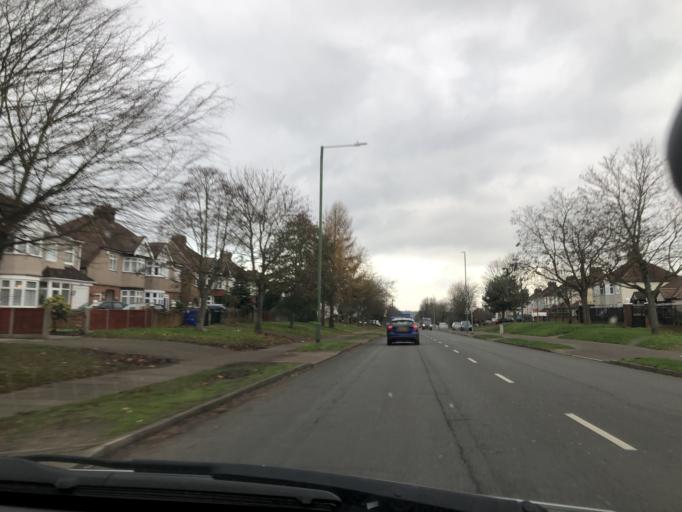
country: GB
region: England
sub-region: Kent
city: Dartford
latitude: 51.4428
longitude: 0.1949
